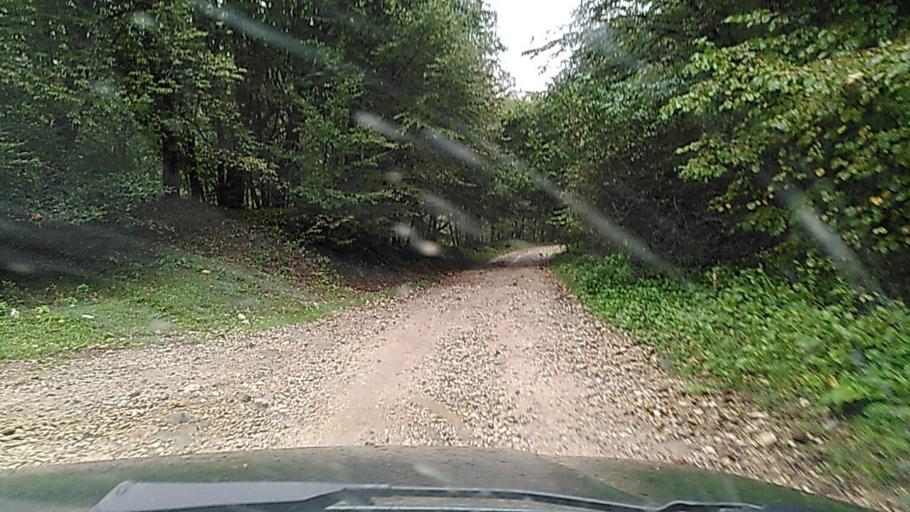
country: RU
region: Kabardino-Balkariya
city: Belaya Rechka
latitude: 43.3960
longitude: 43.4471
